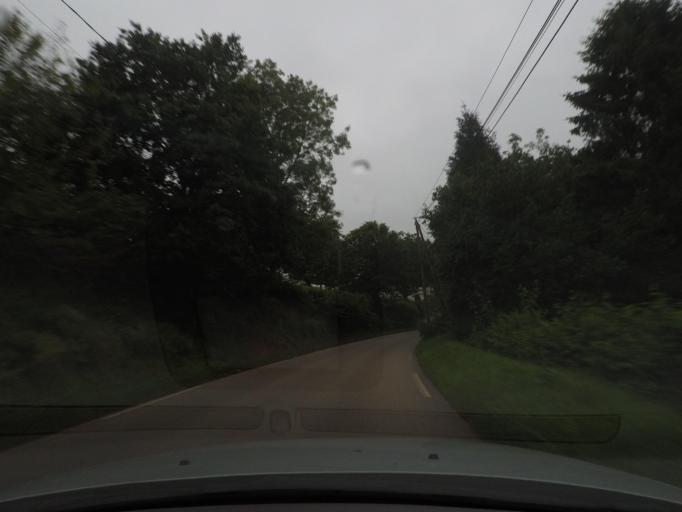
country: FR
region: Haute-Normandie
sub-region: Departement de la Seine-Maritime
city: Fontaine-le-Bourg
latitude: 49.5831
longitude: 1.2318
